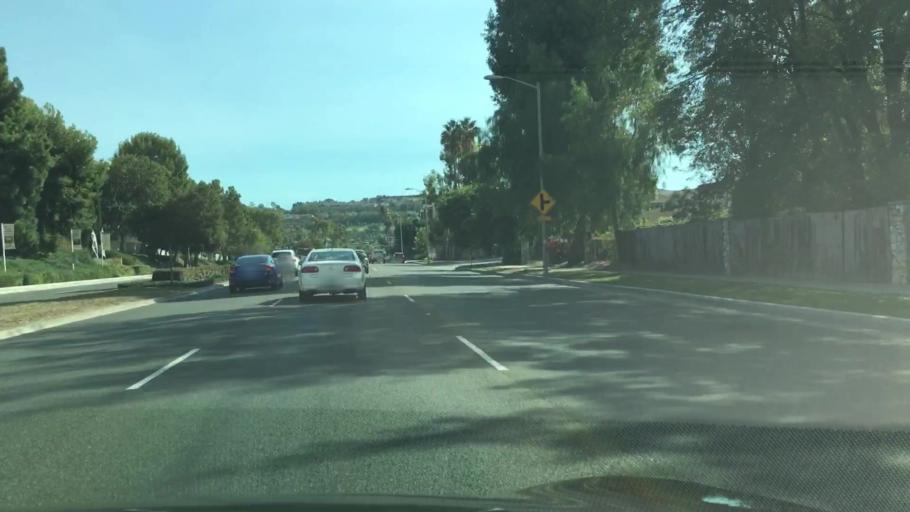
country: US
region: California
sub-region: Los Angeles County
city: East La Mirada
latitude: 33.9227
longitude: -117.9679
